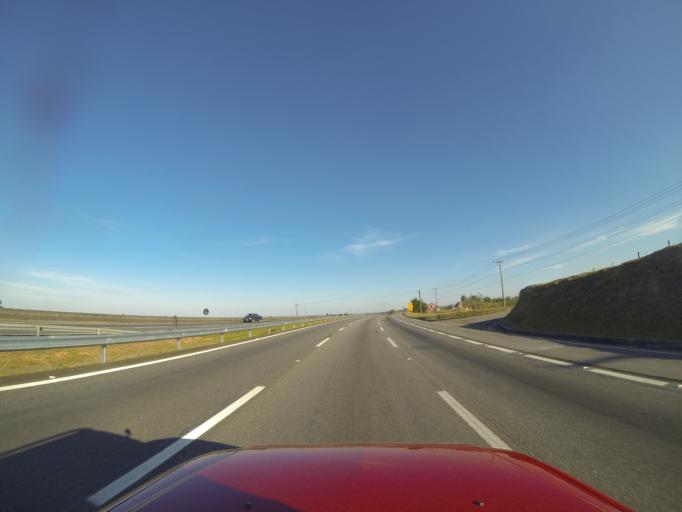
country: BR
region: Sao Paulo
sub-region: Jacarei
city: Jacarei
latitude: -23.2799
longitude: -46.0501
